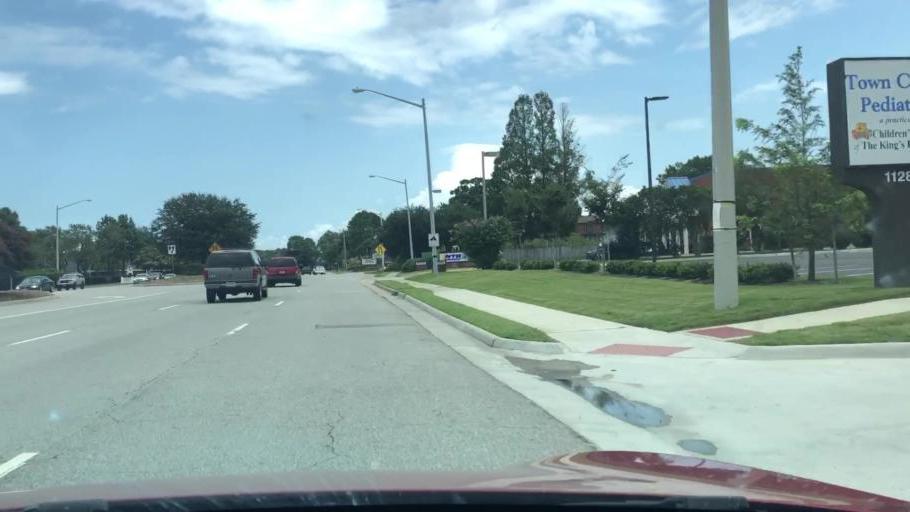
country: US
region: Virginia
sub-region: City of Chesapeake
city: Chesapeake
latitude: 36.8762
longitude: -76.1339
